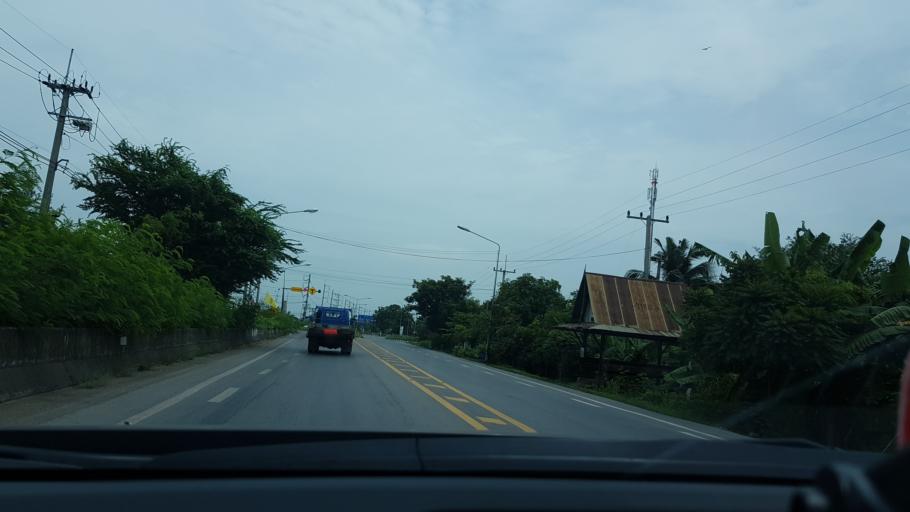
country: TH
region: Pathum Thani
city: Sam Khok
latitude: 14.1287
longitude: 100.5401
